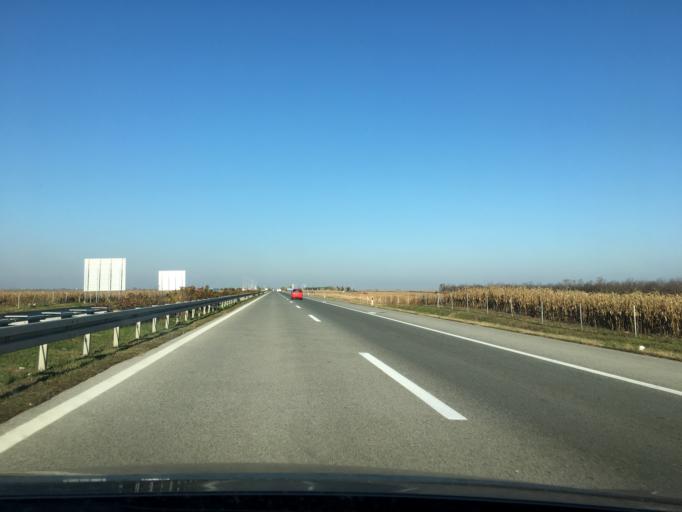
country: RS
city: Rumenka
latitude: 45.3225
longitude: 19.7880
